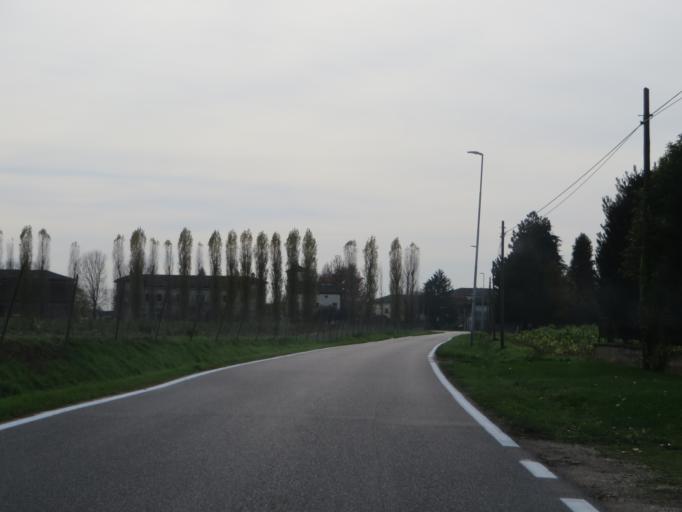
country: IT
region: Veneto
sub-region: Provincia di Verona
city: San Pietro di Morubio
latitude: 45.2516
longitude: 11.2340
